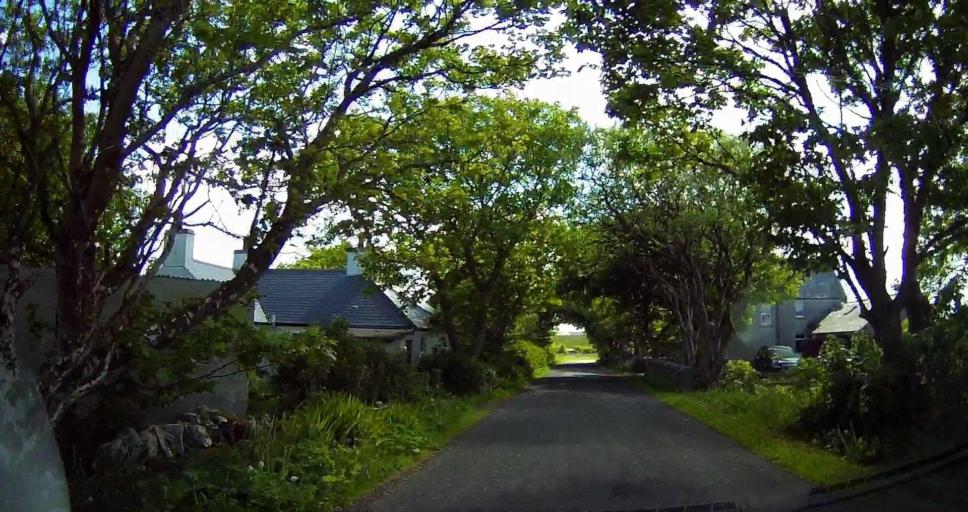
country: GB
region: Scotland
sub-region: Orkney Islands
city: Stromness
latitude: 59.0434
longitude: -3.1841
